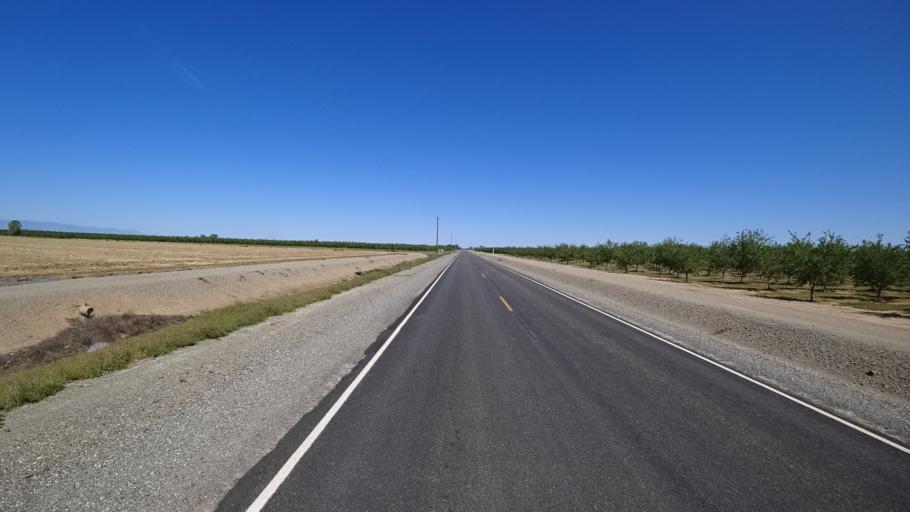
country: US
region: California
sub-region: Glenn County
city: Orland
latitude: 39.6584
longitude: -122.1408
